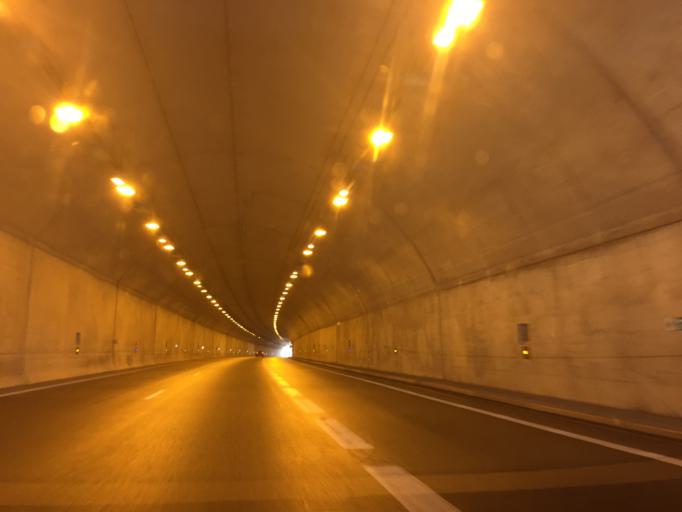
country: FR
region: Limousin
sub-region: Departement de la Correze
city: Cublac
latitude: 45.1657
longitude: 1.2337
